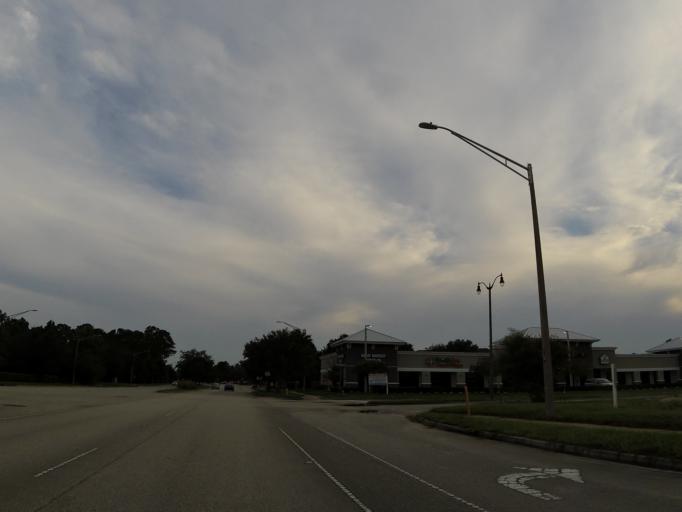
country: US
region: Florida
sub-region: Saint Johns County
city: Ponte Vedra Beach
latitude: 30.2324
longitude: -81.5104
